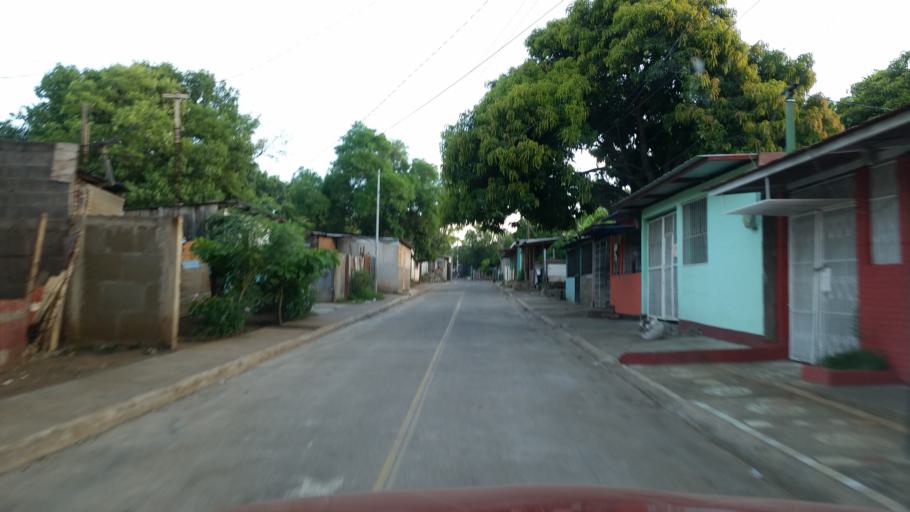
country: NI
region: Managua
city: Managua
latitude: 12.1302
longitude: -86.2874
